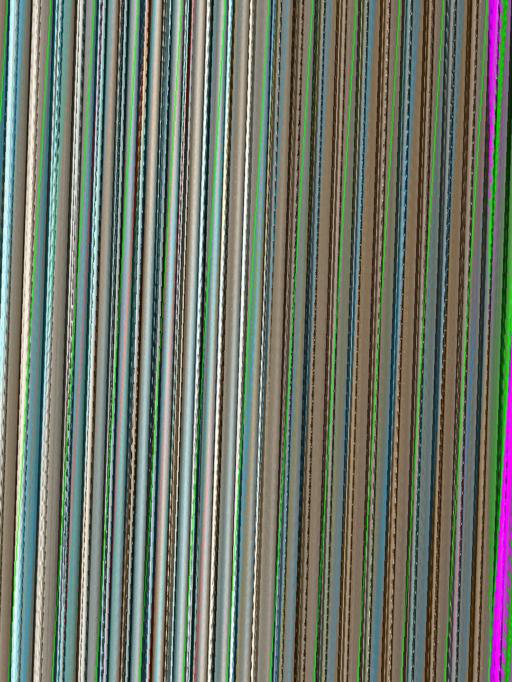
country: RU
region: Moskovskaya
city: Filimonki
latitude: 55.5599
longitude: 37.4111
